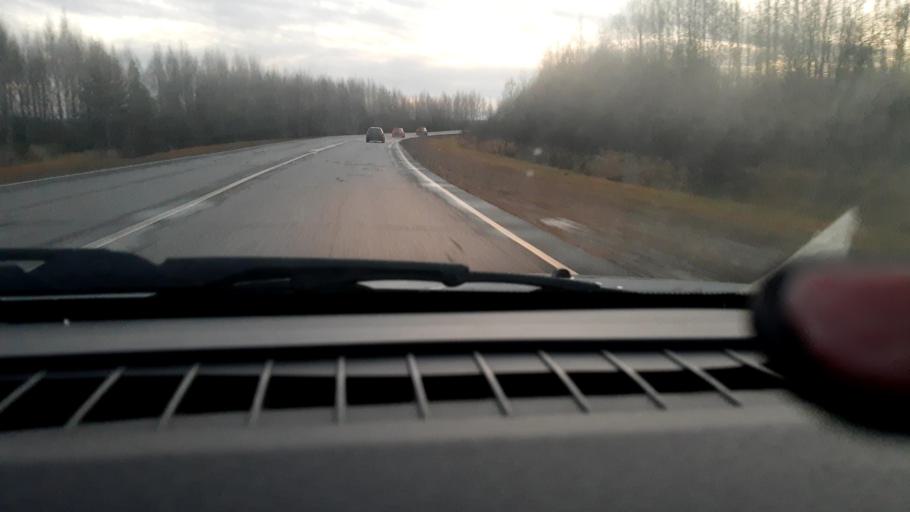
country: RU
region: Nizjnij Novgorod
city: Vladimirskoye
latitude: 56.9619
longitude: 45.1072
